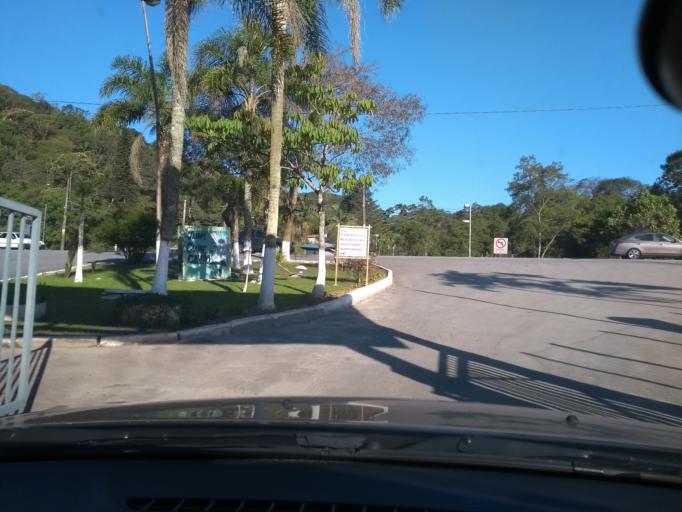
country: BR
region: Sao Paulo
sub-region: Rio Grande Da Serra
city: Rio Grande da Serra
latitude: -23.7640
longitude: -46.4642
